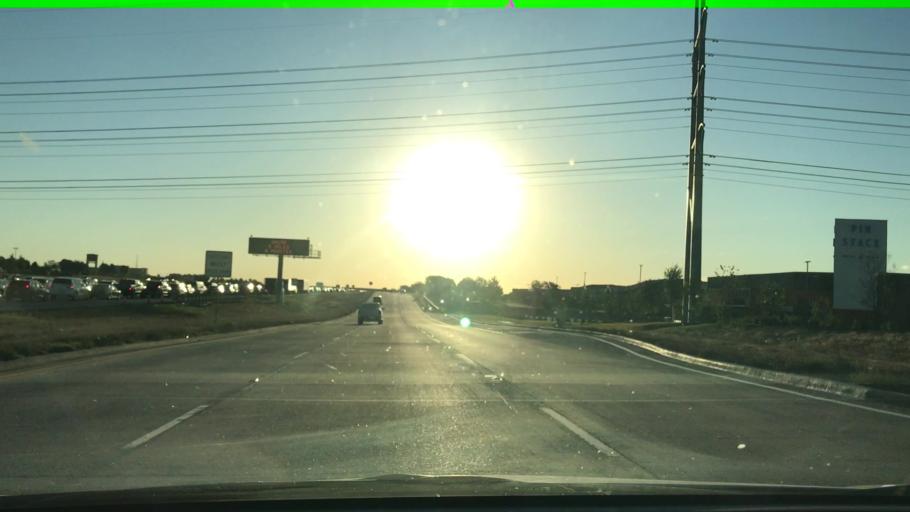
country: US
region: Texas
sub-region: Dallas County
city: Coppell
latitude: 32.9208
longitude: -96.9847
